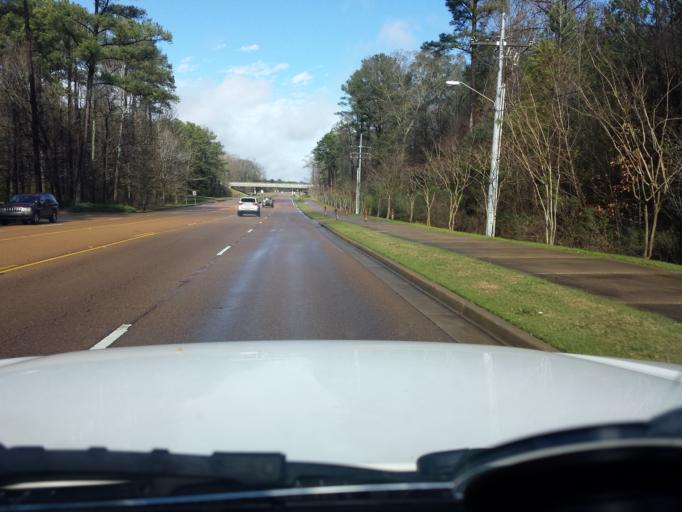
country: US
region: Mississippi
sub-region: Madison County
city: Ridgeland
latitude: 32.4237
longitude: -90.1062
